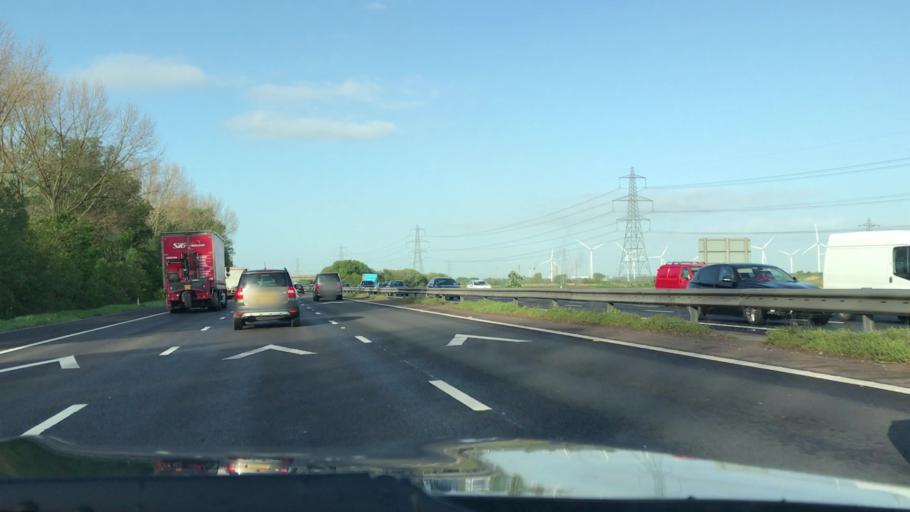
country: GB
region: England
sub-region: Cheshire West and Chester
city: Frodsham
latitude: 53.2944
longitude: -2.7379
